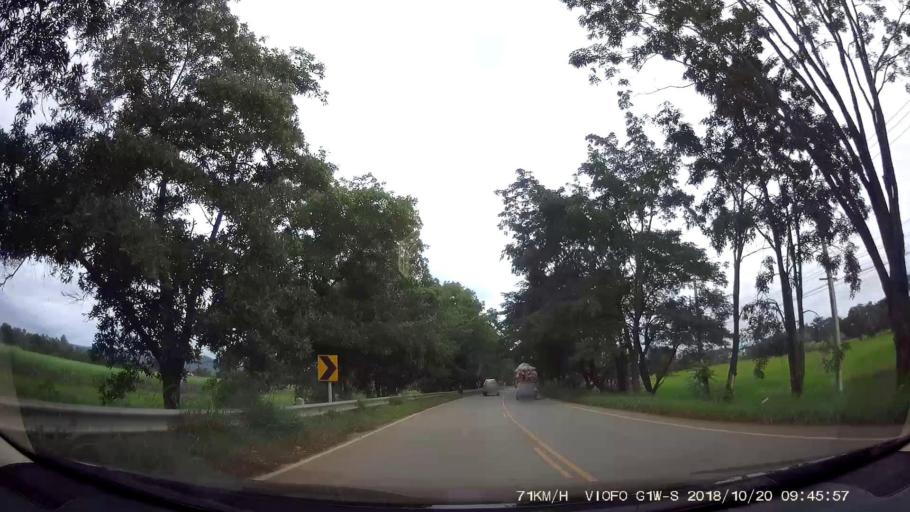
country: TH
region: Chaiyaphum
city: Khon San
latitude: 16.4925
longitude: 101.9306
